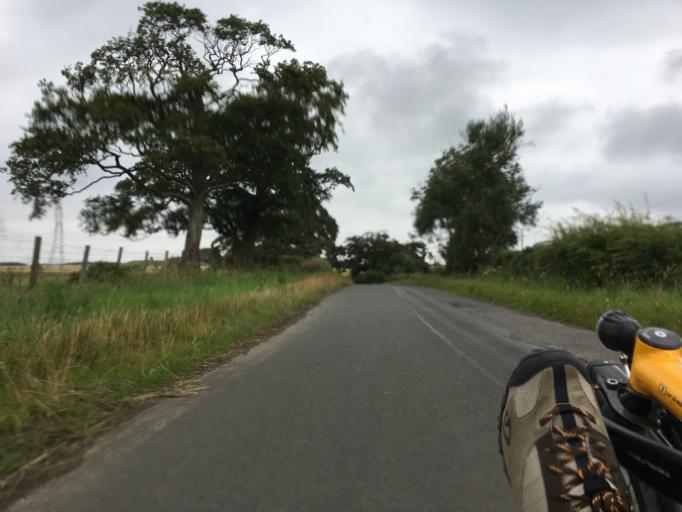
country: GB
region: Scotland
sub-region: West Lothian
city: Mid Calder
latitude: 55.8486
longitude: -3.5127
